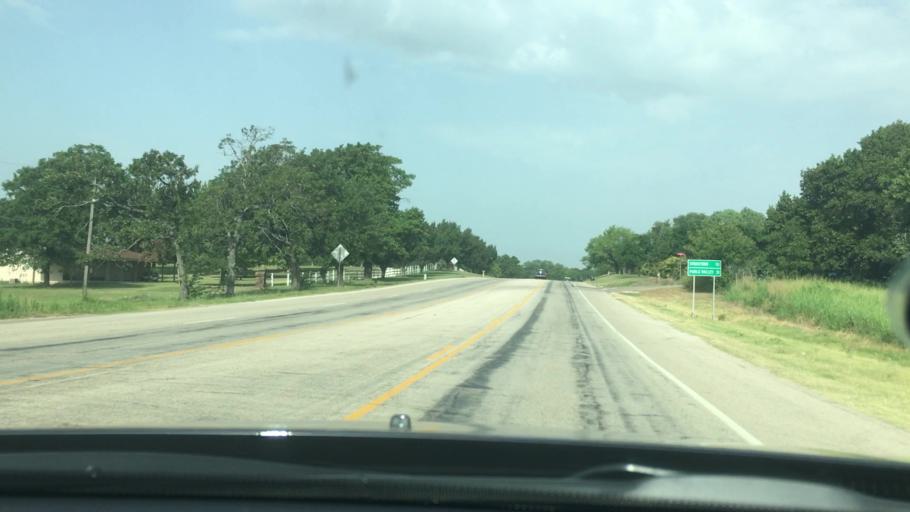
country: US
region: Oklahoma
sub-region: Pontotoc County
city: Ada
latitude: 34.7857
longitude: -96.7300
